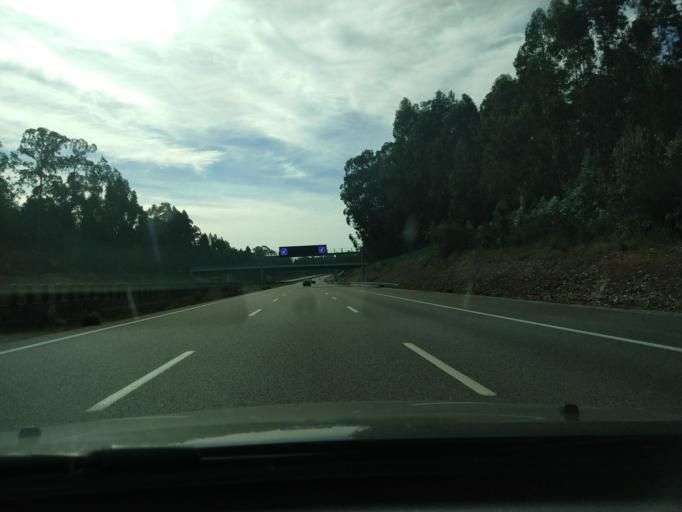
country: PT
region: Aveiro
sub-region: Estarreja
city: Avanca
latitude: 40.8210
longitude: -8.5516
